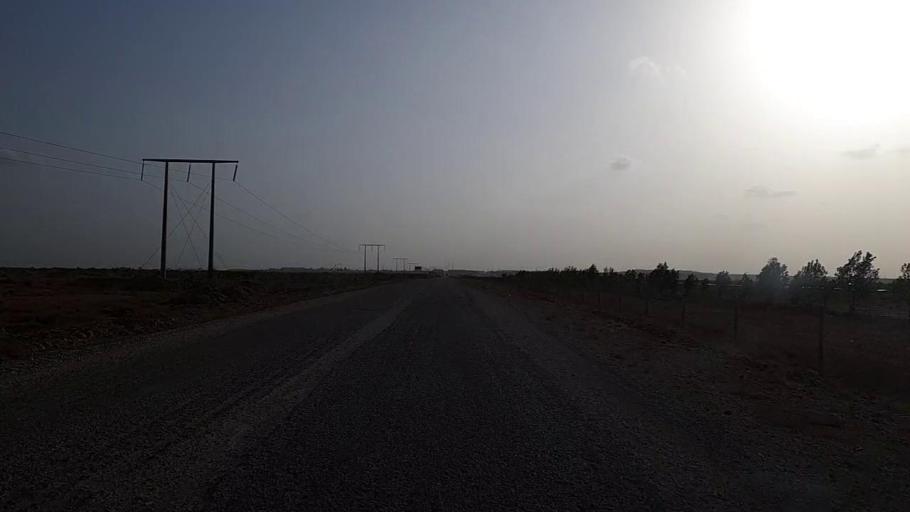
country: PK
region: Sindh
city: Thatta
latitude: 25.1907
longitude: 67.8510
